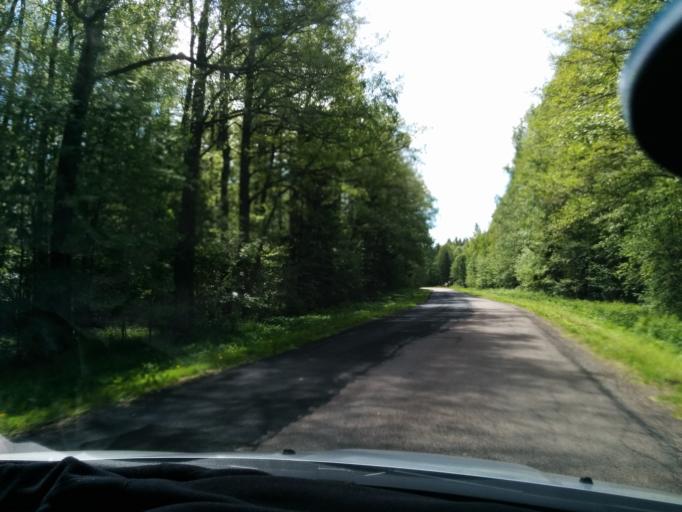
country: EE
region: Harju
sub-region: Loksa linn
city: Loksa
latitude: 59.5942
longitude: 25.9110
